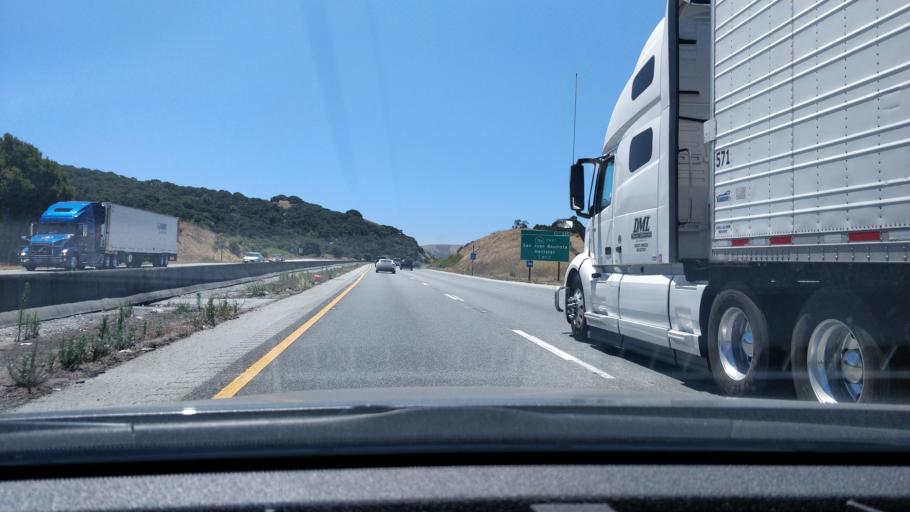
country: US
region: California
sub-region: San Benito County
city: San Juan Bautista
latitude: 36.8733
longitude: -121.5717
